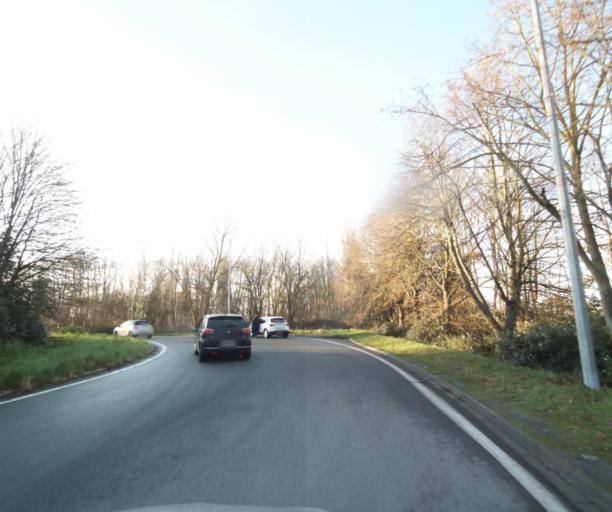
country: FR
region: Nord-Pas-de-Calais
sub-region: Departement du Nord
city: Famars
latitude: 50.3280
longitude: 3.5097
